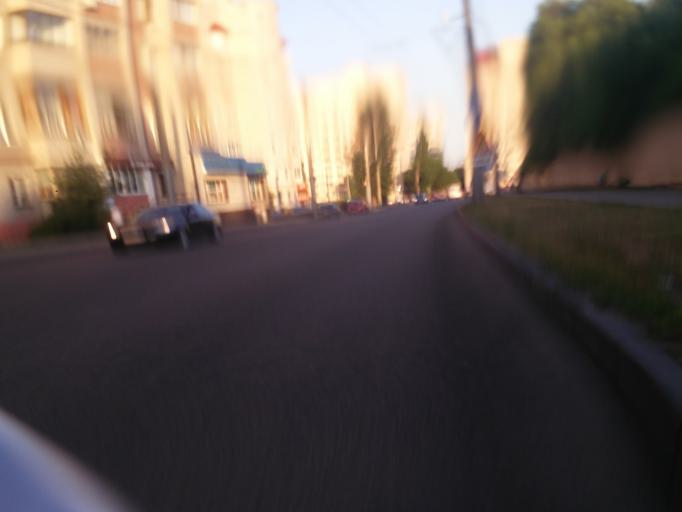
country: RU
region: Voronezj
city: Voronezh
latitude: 51.6490
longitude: 39.1542
